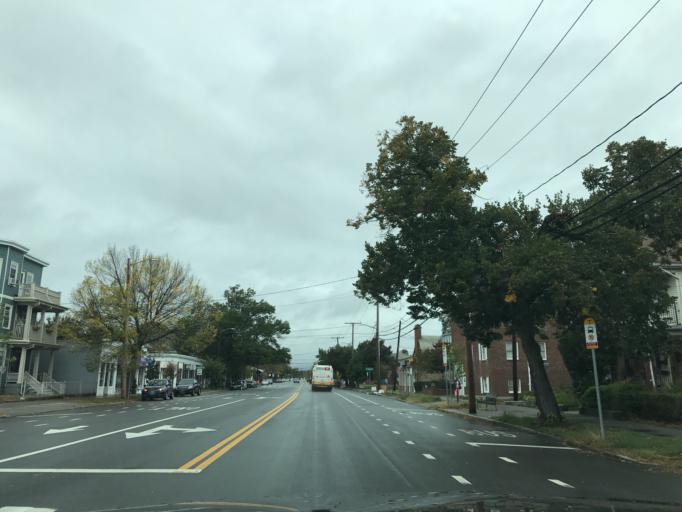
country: US
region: Massachusetts
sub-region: Middlesex County
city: Arlington
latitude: 42.4027
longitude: -71.1384
